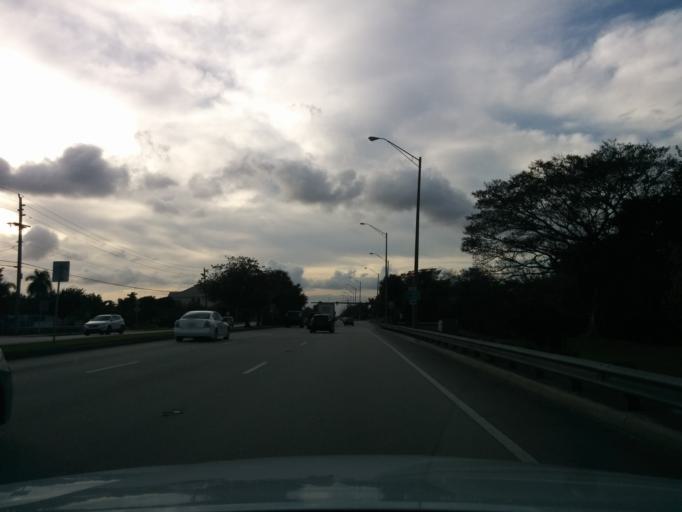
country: US
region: Florida
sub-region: Broward County
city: Davie
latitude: 26.0651
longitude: -80.2354
